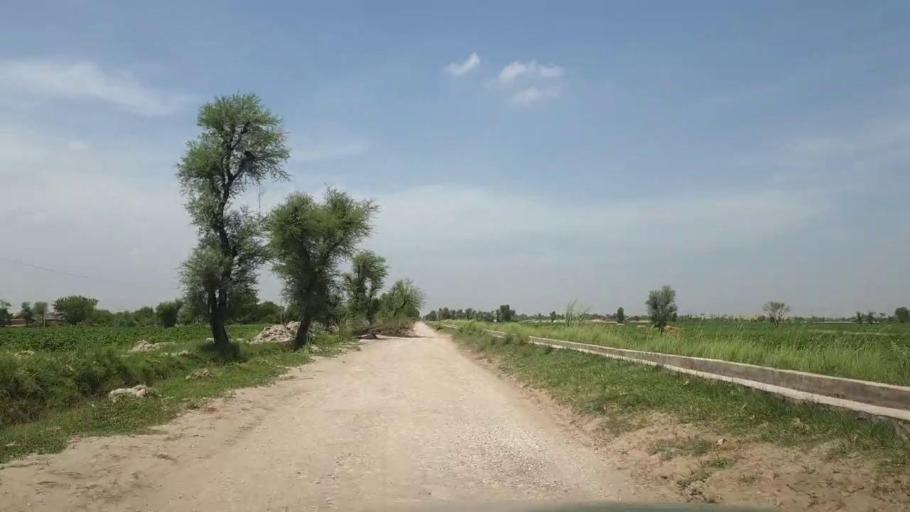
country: PK
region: Sindh
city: Kot Diji
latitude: 27.1357
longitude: 69.0436
